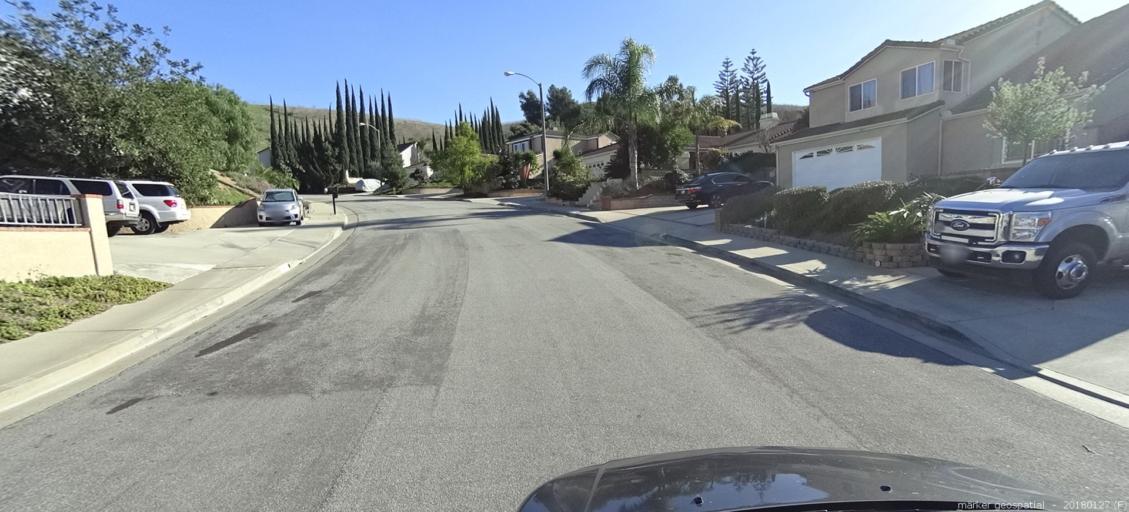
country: US
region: California
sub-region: Los Angeles County
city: Diamond Bar
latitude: 34.0187
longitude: -117.7873
